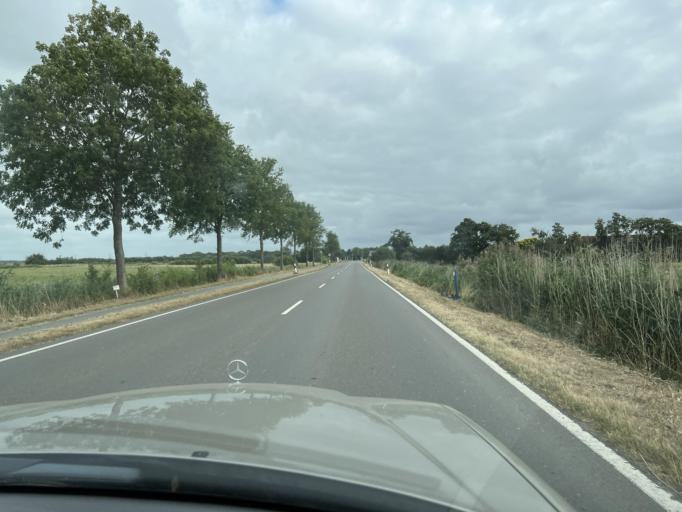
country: DE
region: Schleswig-Holstein
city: Stelle-Wittenwurth
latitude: 54.2613
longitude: 9.0539
